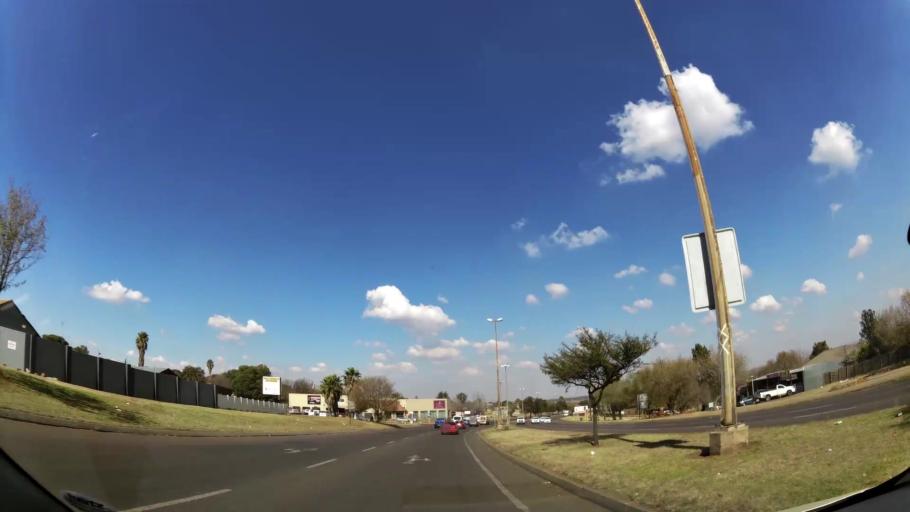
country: ZA
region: Mpumalanga
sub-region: Nkangala District Municipality
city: Witbank
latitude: -25.9056
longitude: 29.2367
